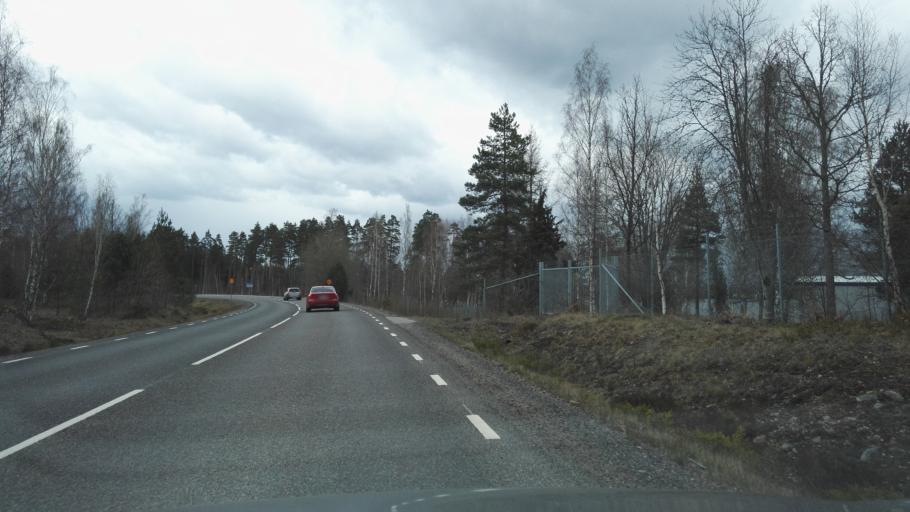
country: SE
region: Kronoberg
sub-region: Vaxjo Kommun
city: Braas
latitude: 57.0572
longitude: 15.0383
